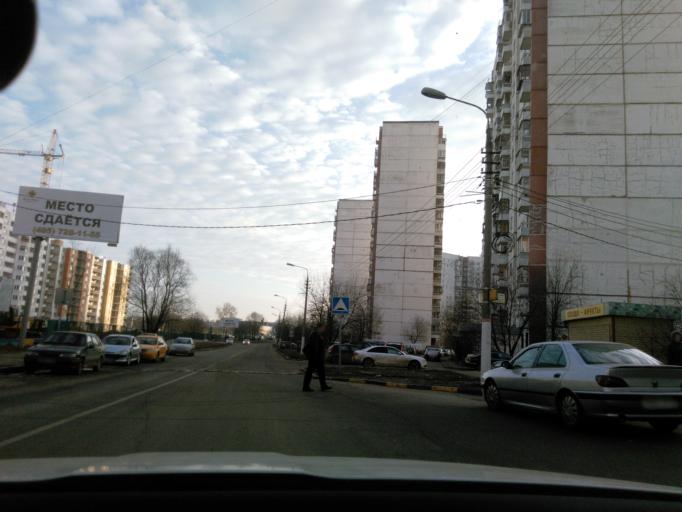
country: RU
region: Moscow
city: Khimki
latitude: 55.9034
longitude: 37.4037
